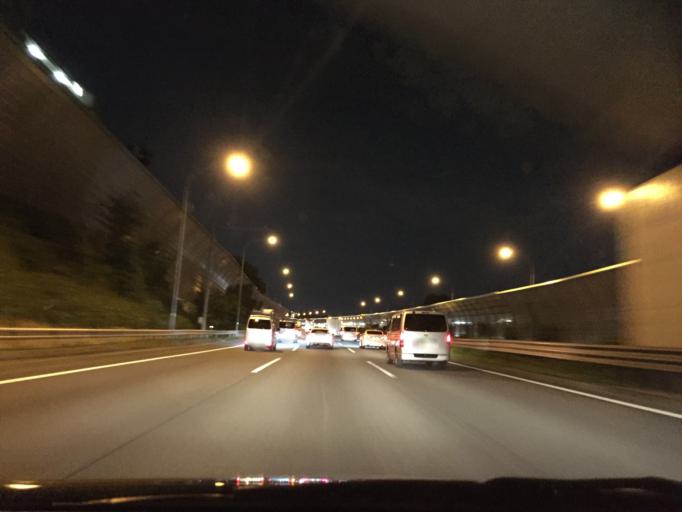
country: JP
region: Tokyo
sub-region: Machida-shi
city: Machida
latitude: 35.5275
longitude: 139.5129
